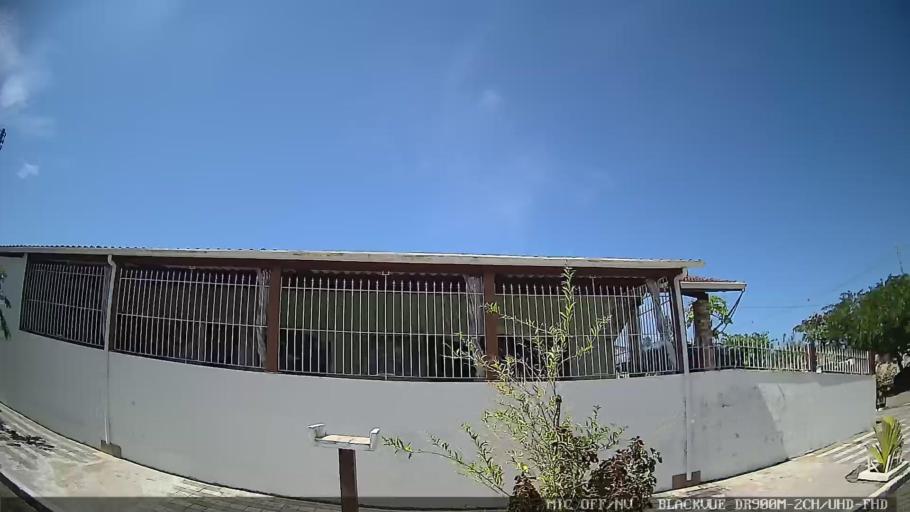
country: BR
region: Sao Paulo
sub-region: Peruibe
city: Peruibe
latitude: -24.3022
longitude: -46.9839
